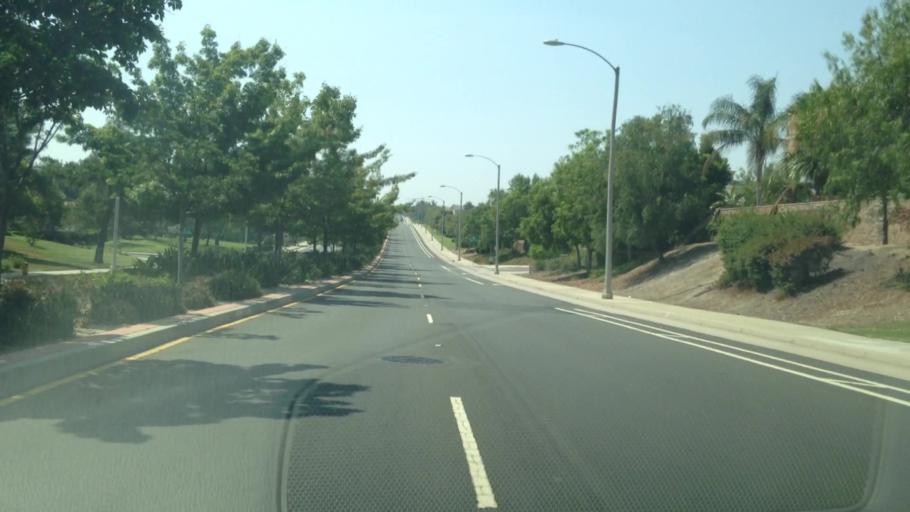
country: US
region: California
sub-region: Riverside County
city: Woodcrest
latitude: 33.9119
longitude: -117.3299
